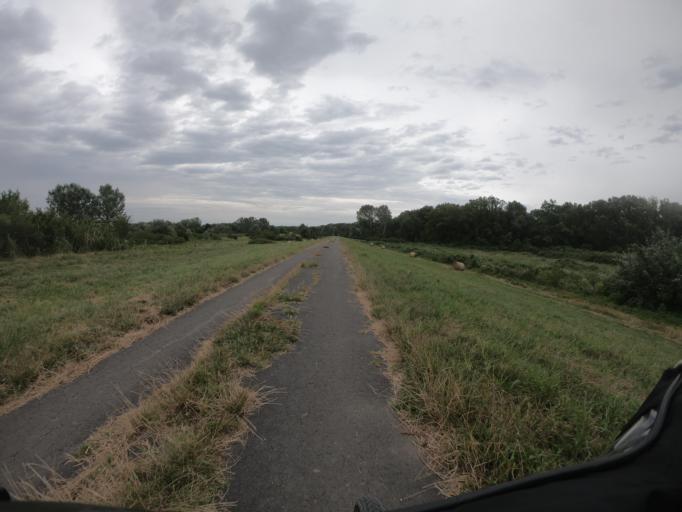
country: HU
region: Hajdu-Bihar
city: Tiszacsege
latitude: 47.7208
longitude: 20.9490
